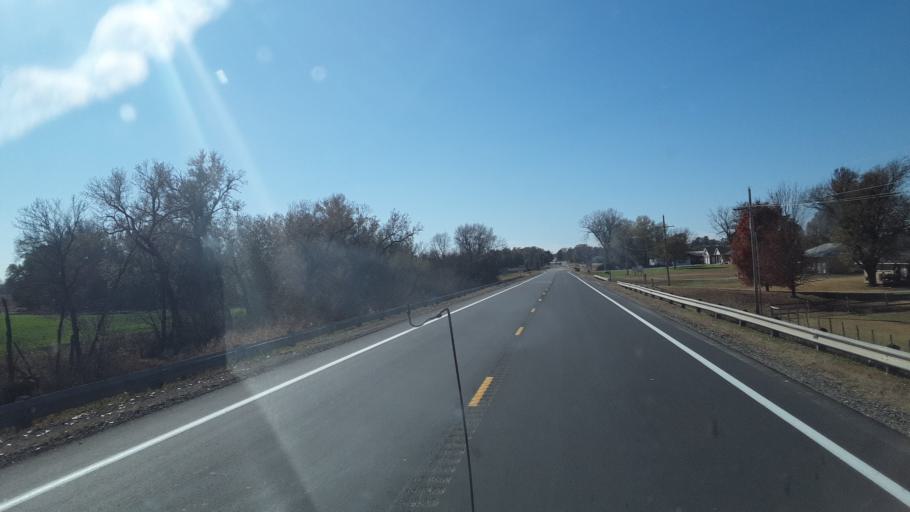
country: US
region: Kansas
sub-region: Rice County
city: Lyons
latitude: 38.3547
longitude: -98.1796
